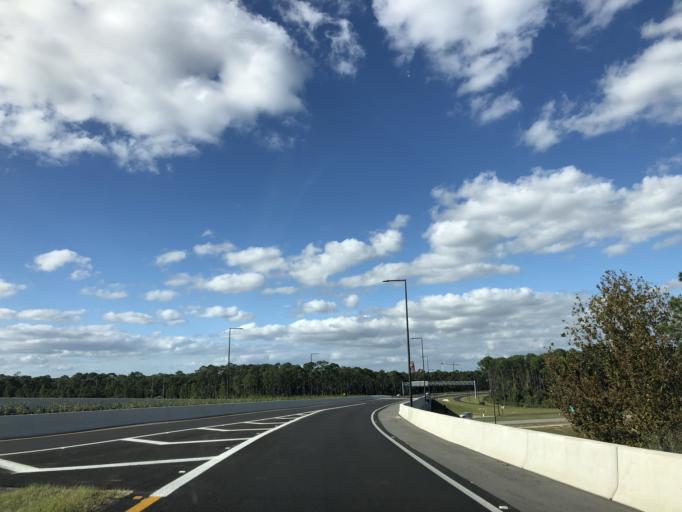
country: US
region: Florida
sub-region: Osceola County
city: Celebration
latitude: 28.3483
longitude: -81.5505
